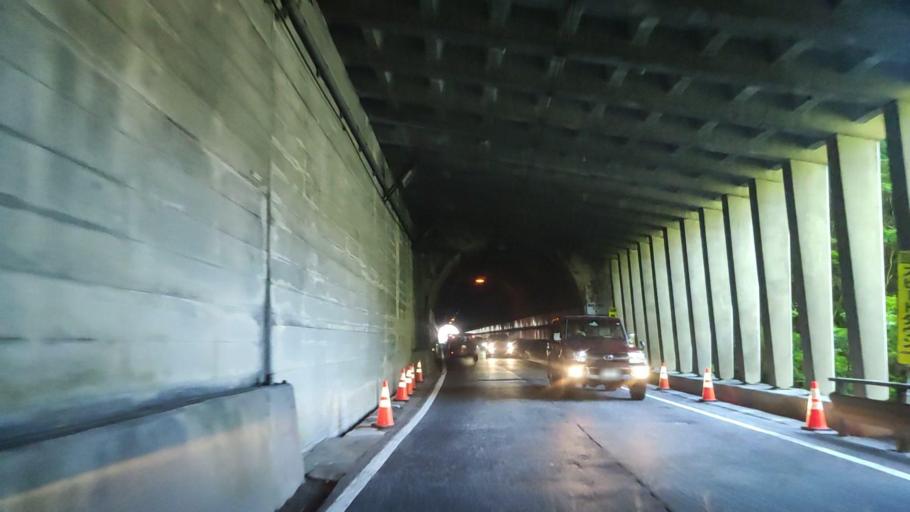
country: JP
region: Nagano
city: Toyoshina
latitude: 36.1341
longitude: 137.7248
